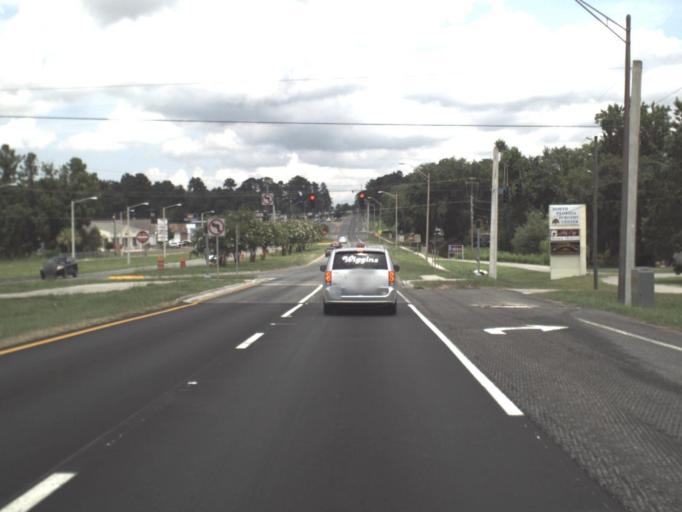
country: US
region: Florida
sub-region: Columbia County
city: Lake City
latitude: 30.1676
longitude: -82.6411
